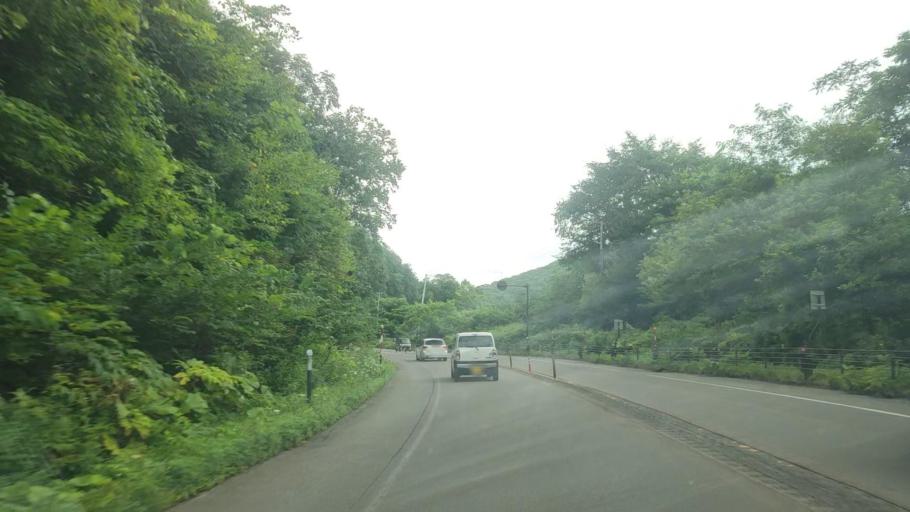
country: JP
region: Hokkaido
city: Nanae
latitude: 41.9723
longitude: 140.6496
